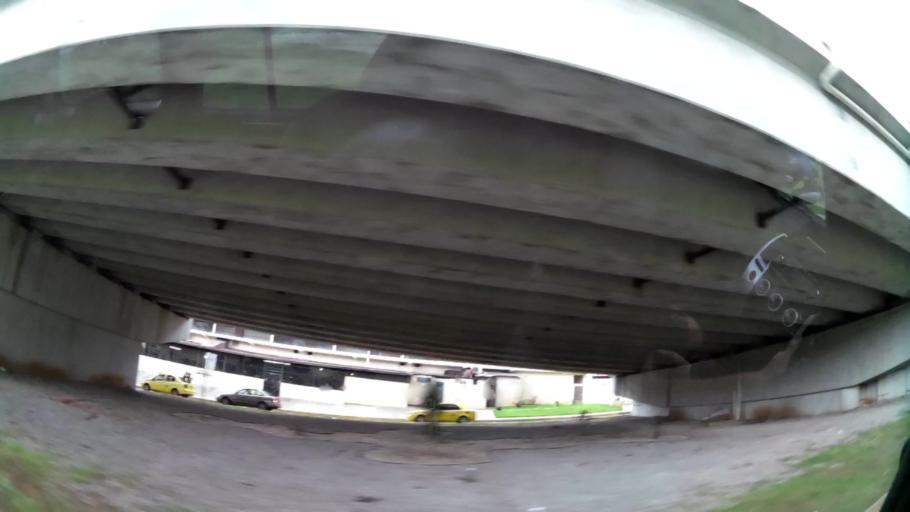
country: PA
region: Panama
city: Tocumen
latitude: 9.0640
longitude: -79.4184
